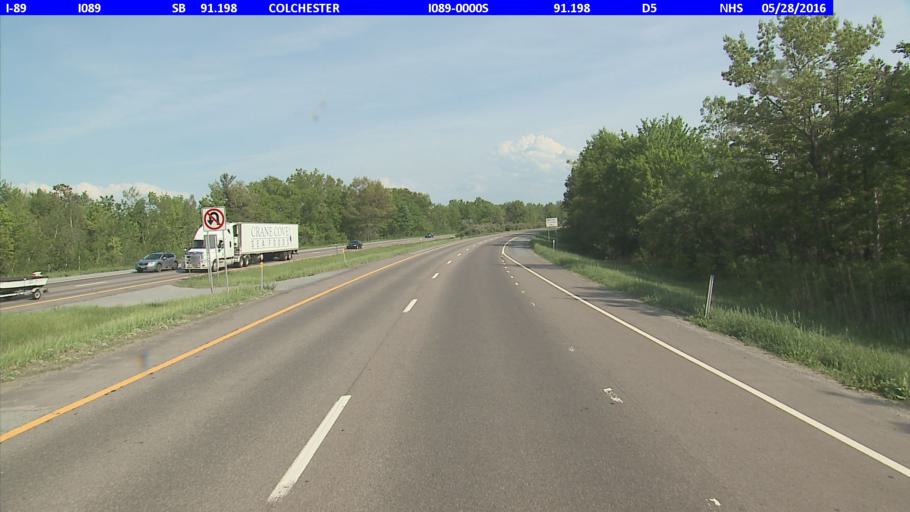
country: US
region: Vermont
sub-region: Chittenden County
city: Winooski
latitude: 44.5032
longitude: -73.1766
